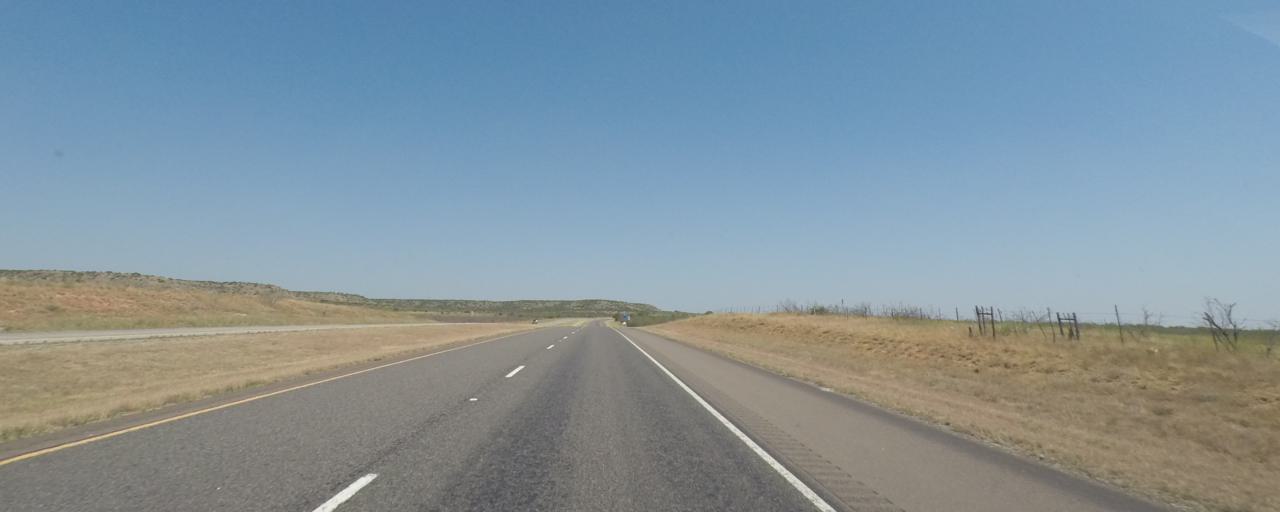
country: US
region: Texas
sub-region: Dickens County
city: Dickens
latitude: 33.6346
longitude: -100.8881
